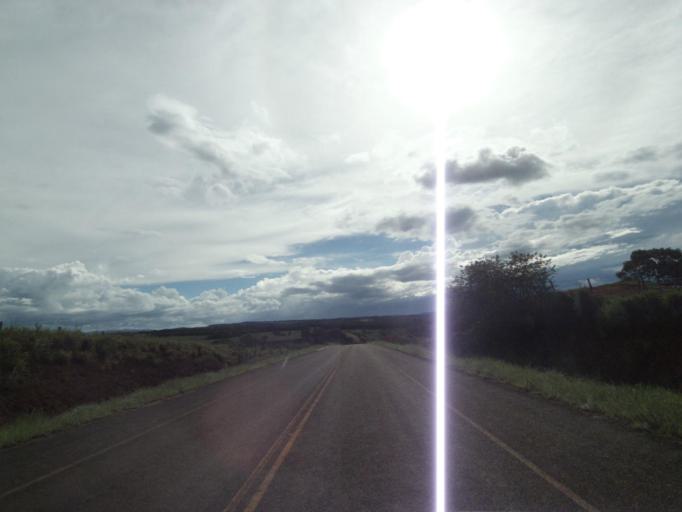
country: BR
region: Goias
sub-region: Jaragua
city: Jaragua
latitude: -15.8687
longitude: -49.4086
